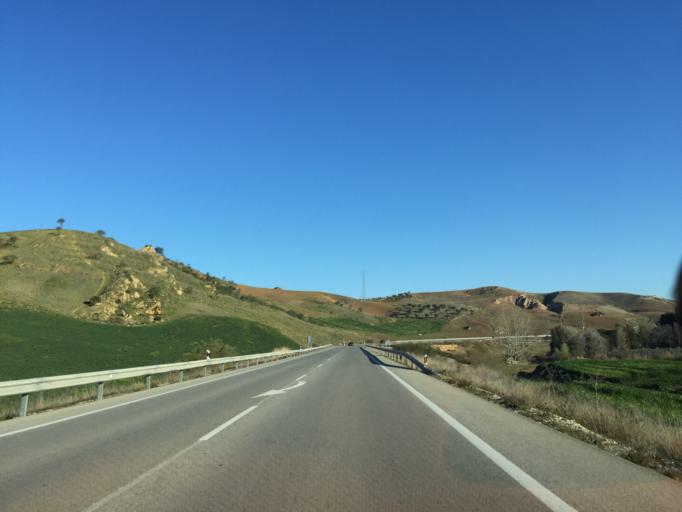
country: ES
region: Andalusia
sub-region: Provincia de Malaga
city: Ardales
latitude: 36.8918
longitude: -4.8482
